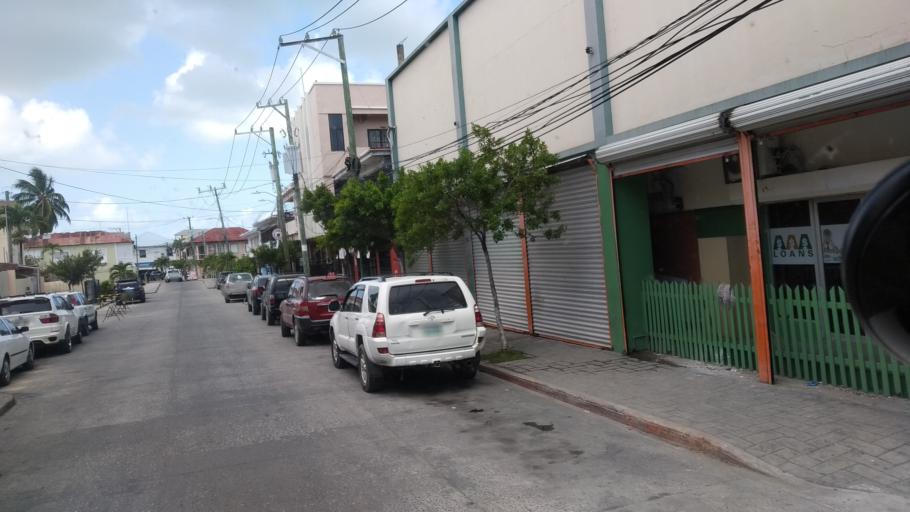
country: BZ
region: Belize
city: Belize City
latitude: 17.4967
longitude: -88.1856
